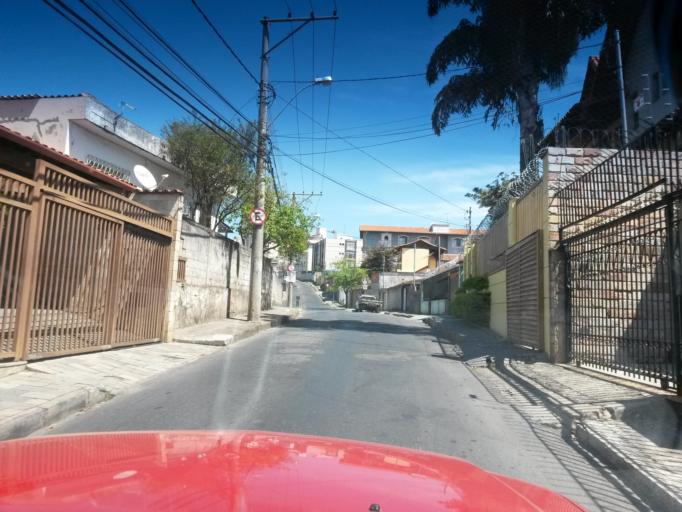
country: BR
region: Minas Gerais
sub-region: Belo Horizonte
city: Belo Horizonte
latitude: -19.8951
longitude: -43.9691
